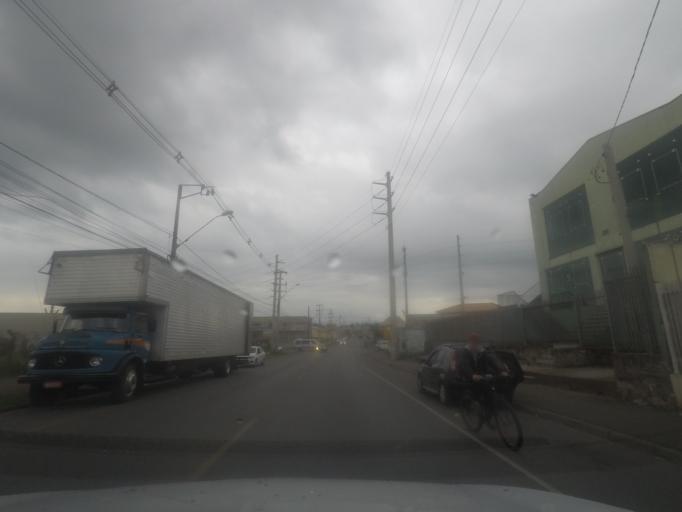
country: BR
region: Parana
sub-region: Sao Jose Dos Pinhais
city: Sao Jose dos Pinhais
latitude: -25.5563
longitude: -49.2541
